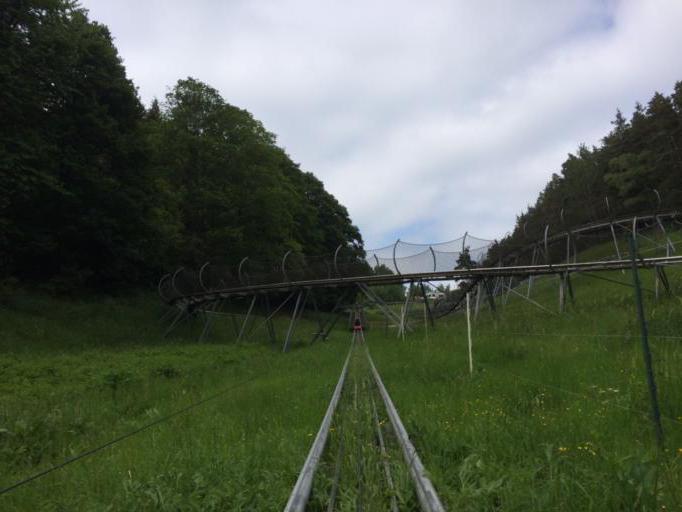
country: DE
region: Thuringia
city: Doschnitz
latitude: 50.6252
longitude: 11.2566
